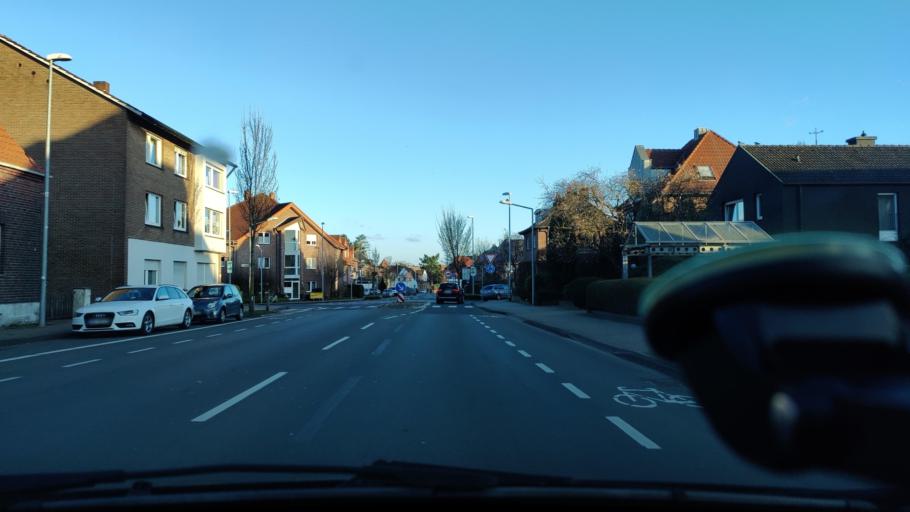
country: DE
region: North Rhine-Westphalia
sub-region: Regierungsbezirk Munster
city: Dulmen
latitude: 51.8342
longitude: 7.2741
